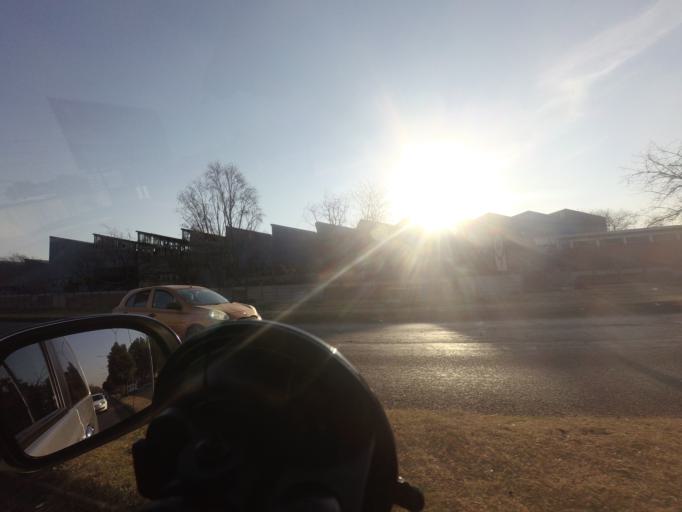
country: ZA
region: Gauteng
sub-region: Sedibeng District Municipality
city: Vereeniging
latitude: -26.6682
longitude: 27.9404
